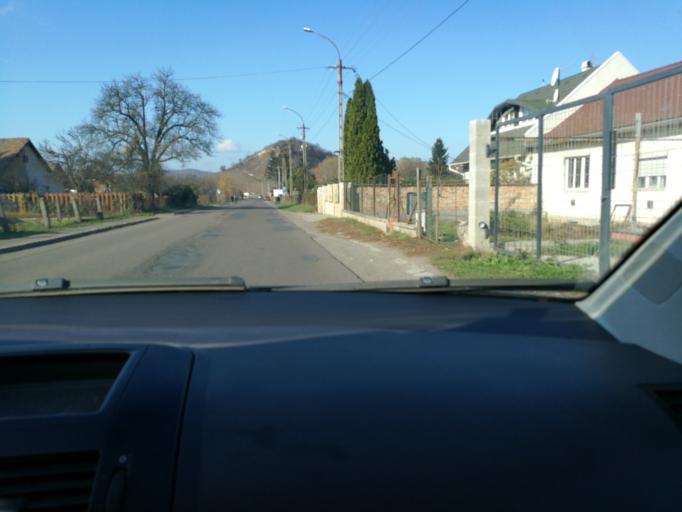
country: HU
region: Nograd
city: Batonyterenye
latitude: 47.9790
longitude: 19.8163
